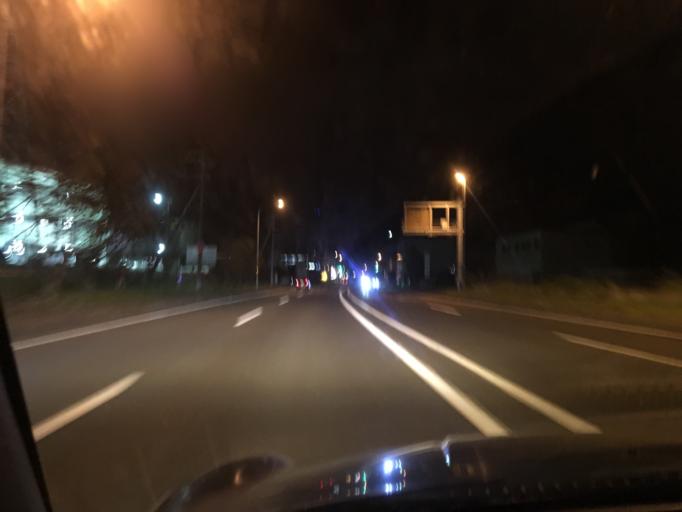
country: JP
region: Hokkaido
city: Muroran
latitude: 42.3522
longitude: 141.0052
